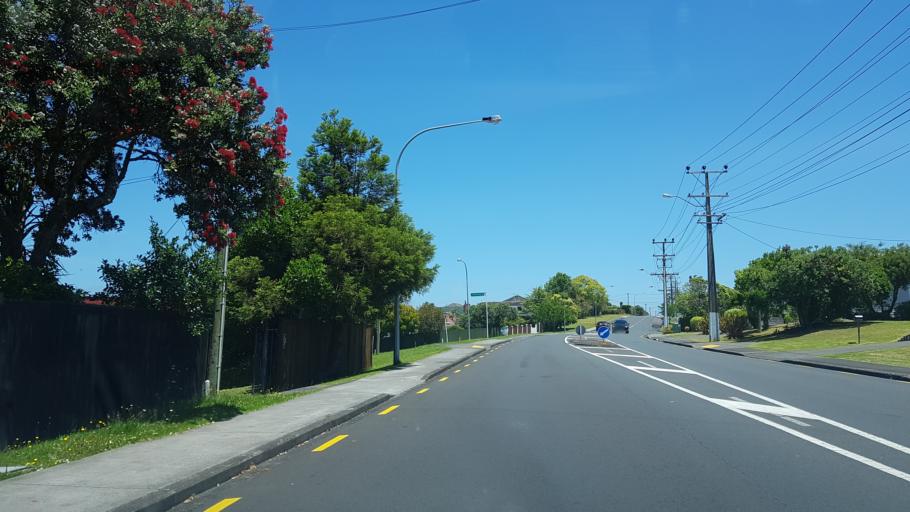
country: NZ
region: Auckland
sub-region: Auckland
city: North Shore
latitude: -36.7892
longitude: 174.7374
